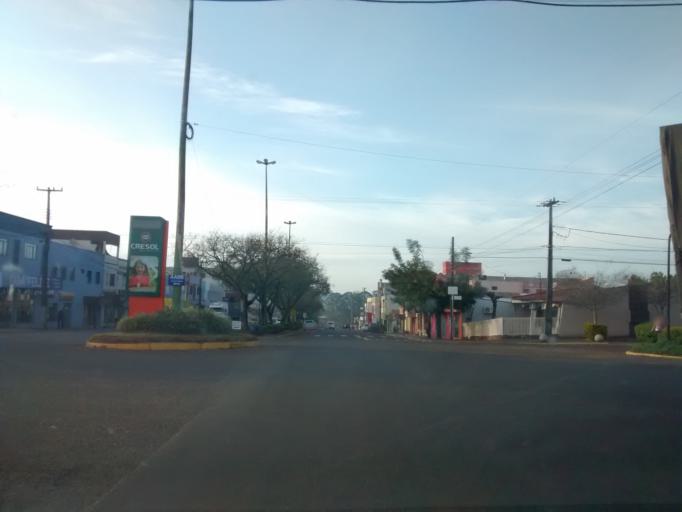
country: BR
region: Parana
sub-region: Francisco Beltrao
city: Francisco Beltrao
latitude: -26.1480
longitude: -53.0239
